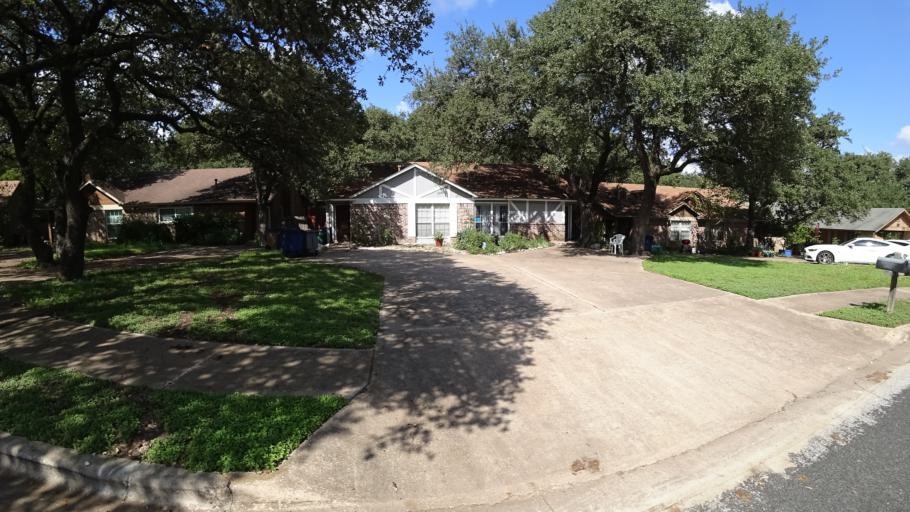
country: US
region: Texas
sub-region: Travis County
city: Onion Creek
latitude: 30.1981
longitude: -97.8014
